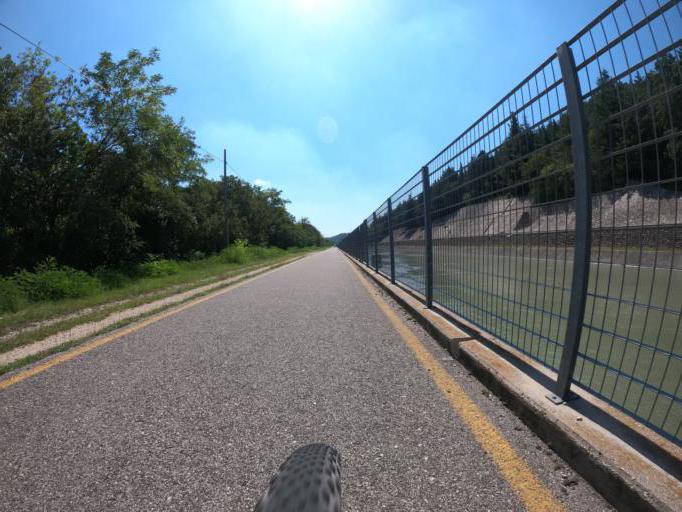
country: IT
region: Veneto
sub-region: Provincia di Verona
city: Volargne
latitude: 45.5255
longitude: 10.7968
